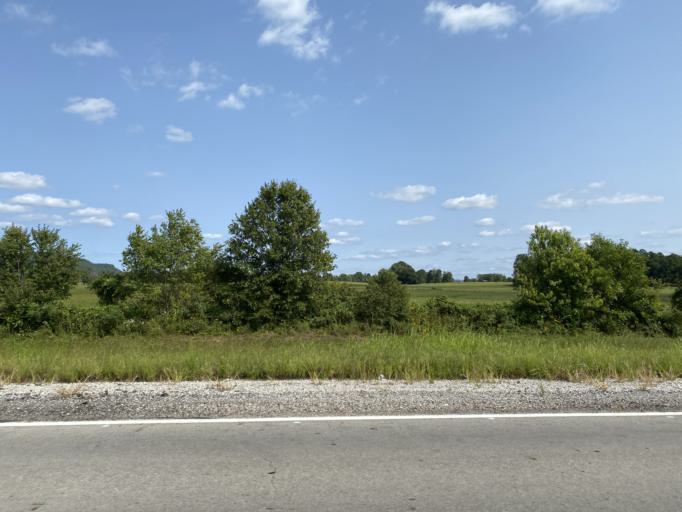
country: US
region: Kentucky
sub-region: Marion County
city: Lebanon
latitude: 37.5053
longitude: -85.2934
